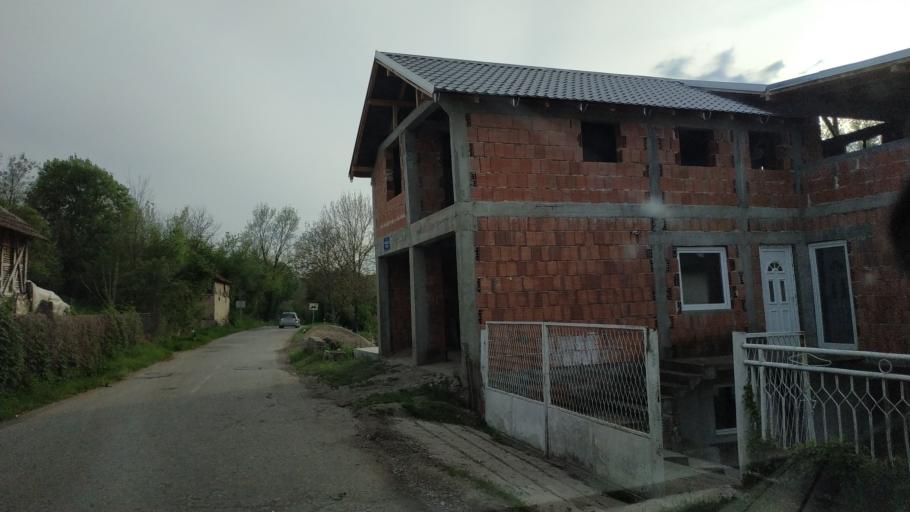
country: RS
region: Central Serbia
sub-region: Nisavski Okrug
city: Aleksinac
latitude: 43.4829
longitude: 21.8168
